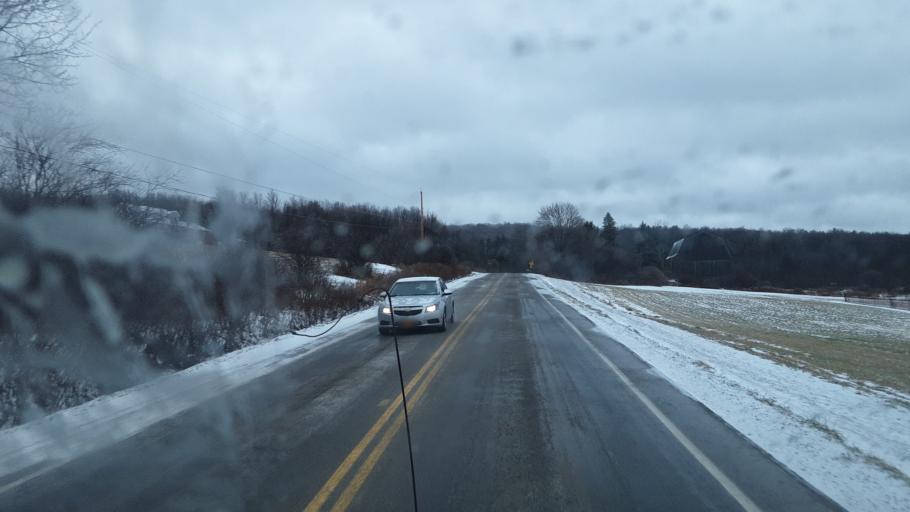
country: US
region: New York
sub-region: Allegany County
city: Friendship
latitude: 42.2486
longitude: -78.1476
